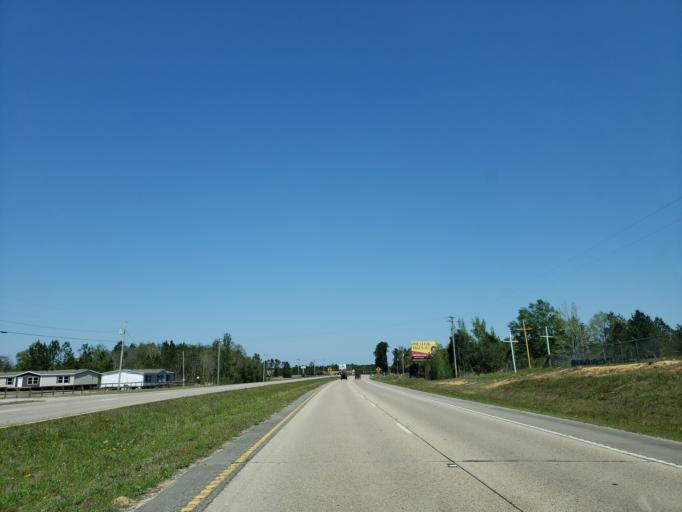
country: US
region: Mississippi
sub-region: Harrison County
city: Lyman
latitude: 30.5482
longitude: -89.1196
